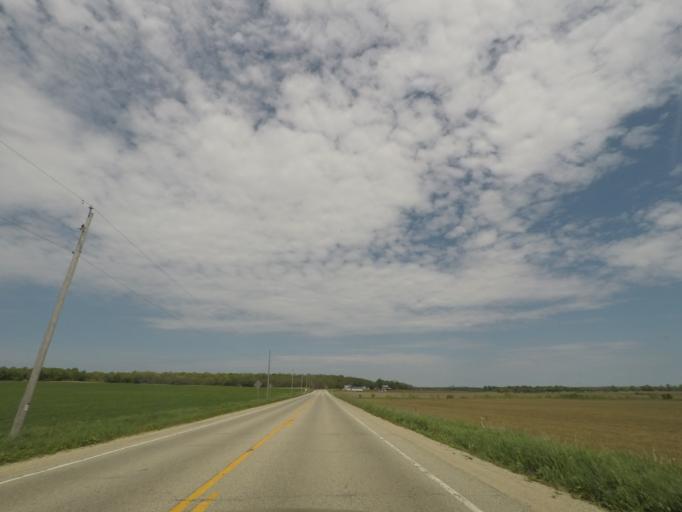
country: US
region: Wisconsin
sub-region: Rock County
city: Evansville
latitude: 42.7190
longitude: -89.2888
